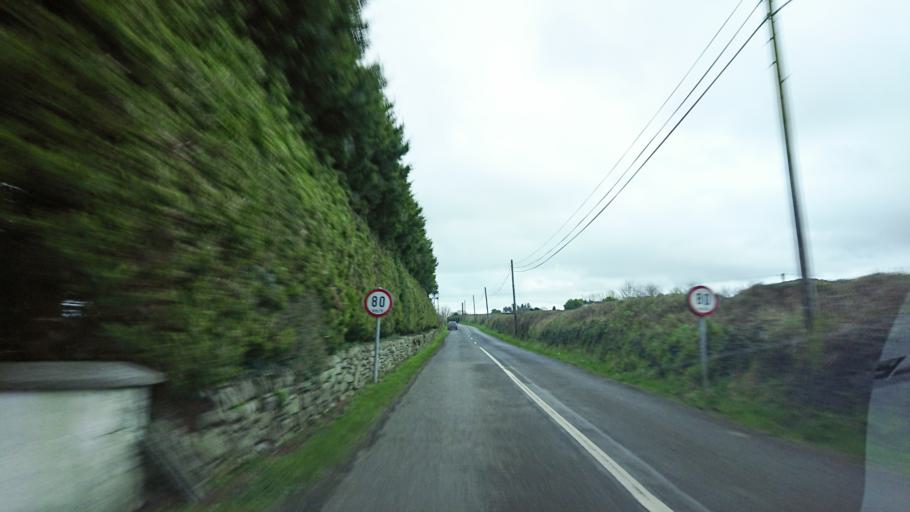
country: IE
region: Munster
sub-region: Waterford
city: Portlaw
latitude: 52.1722
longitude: -7.3978
